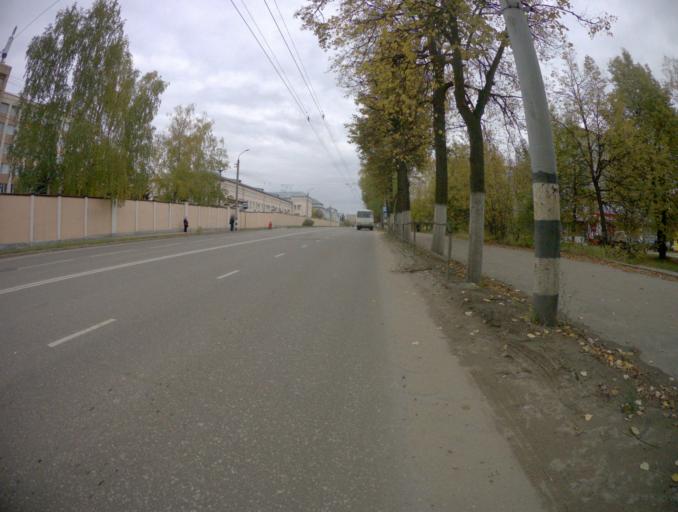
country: RU
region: Vladimir
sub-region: Kovrovskiy Rayon
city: Kovrov
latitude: 56.3654
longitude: 41.3277
